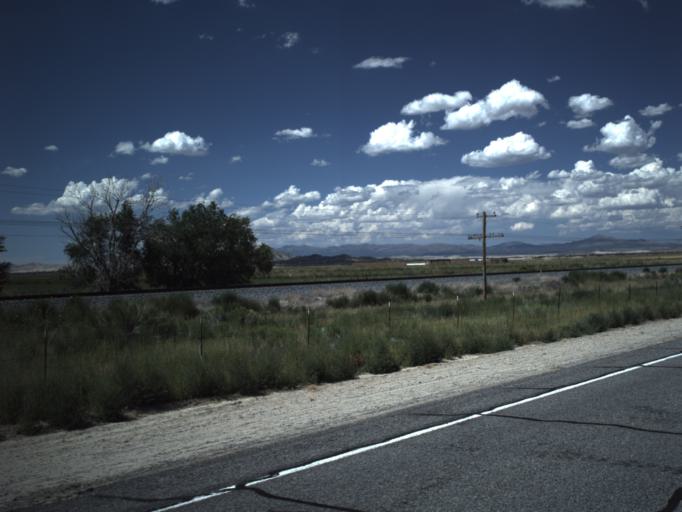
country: US
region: Utah
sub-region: Millard County
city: Delta
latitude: 39.5453
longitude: -112.3599
